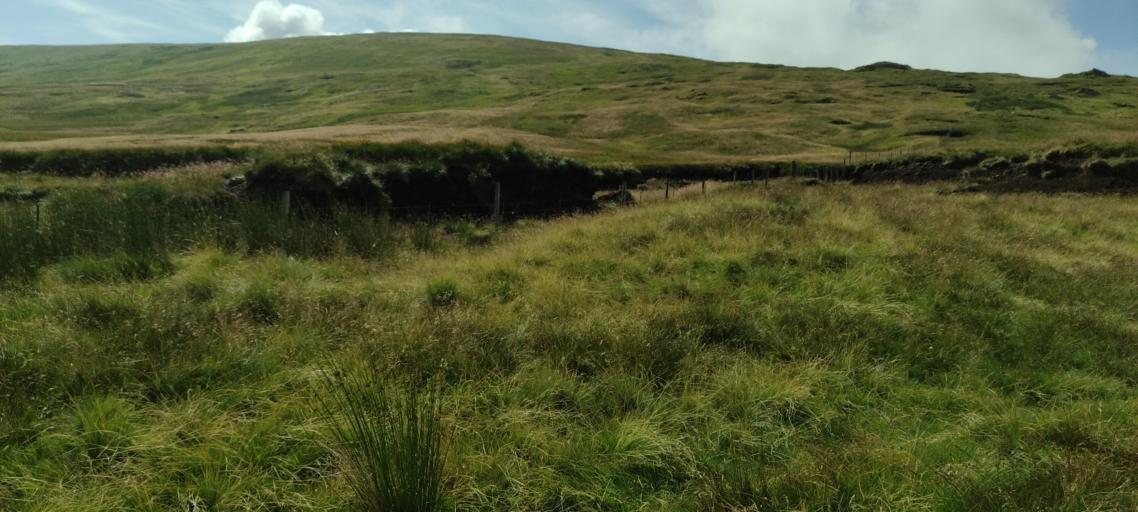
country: GB
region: England
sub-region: Cumbria
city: Windermere
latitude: 54.4721
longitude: -2.7963
